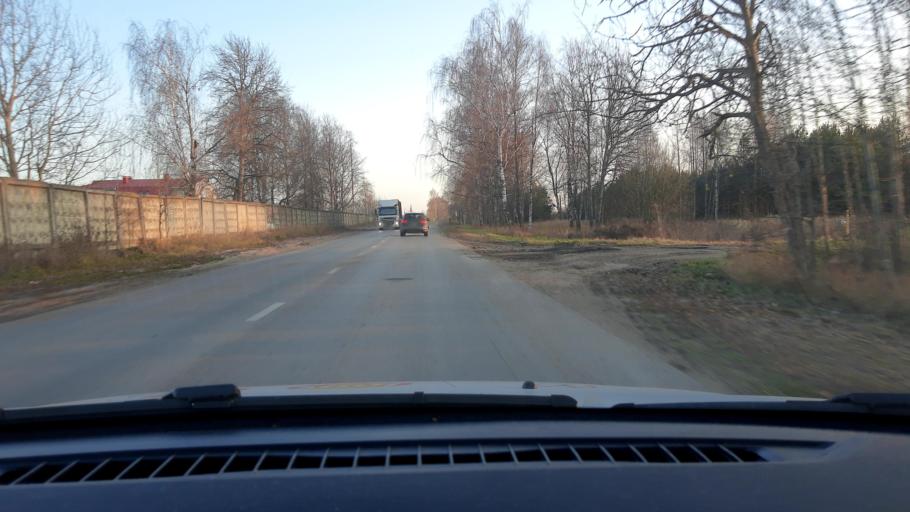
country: RU
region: Nizjnij Novgorod
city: Volodarsk
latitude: 56.2452
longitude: 43.1795
